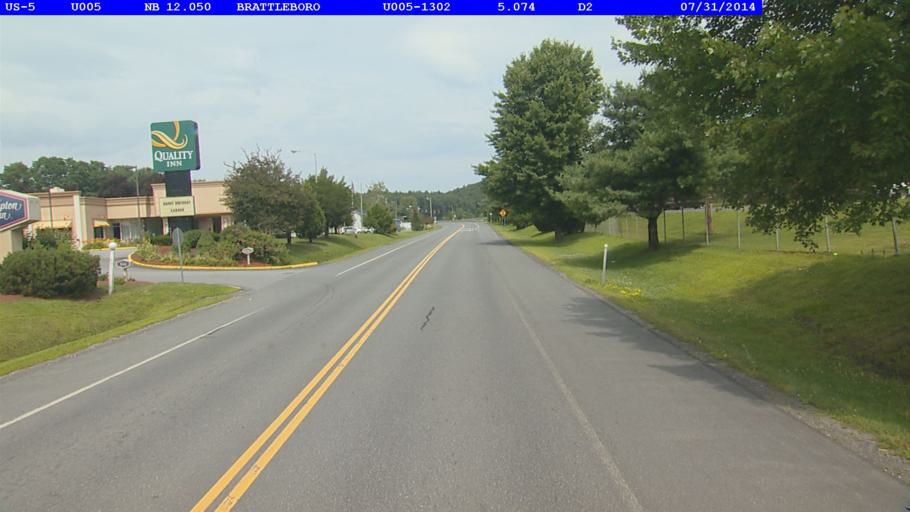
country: US
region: Vermont
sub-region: Windham County
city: Brattleboro
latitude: 42.8908
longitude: -72.5528
